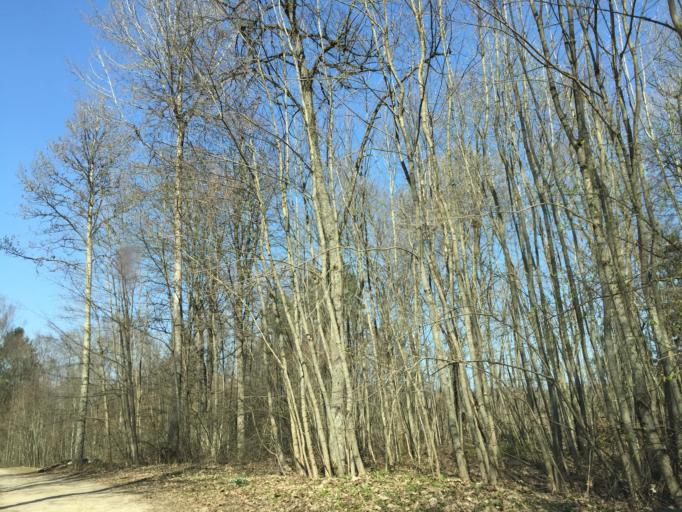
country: LV
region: Malpils
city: Malpils
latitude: 57.0072
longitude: 24.9720
